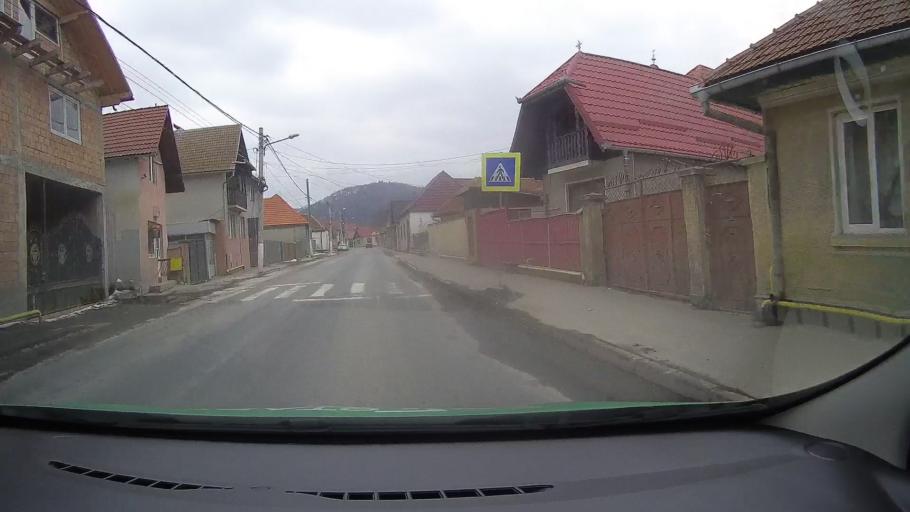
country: RO
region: Brasov
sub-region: Comuna Zarnesti
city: Tohanu Nou
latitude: 45.5762
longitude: 25.3727
